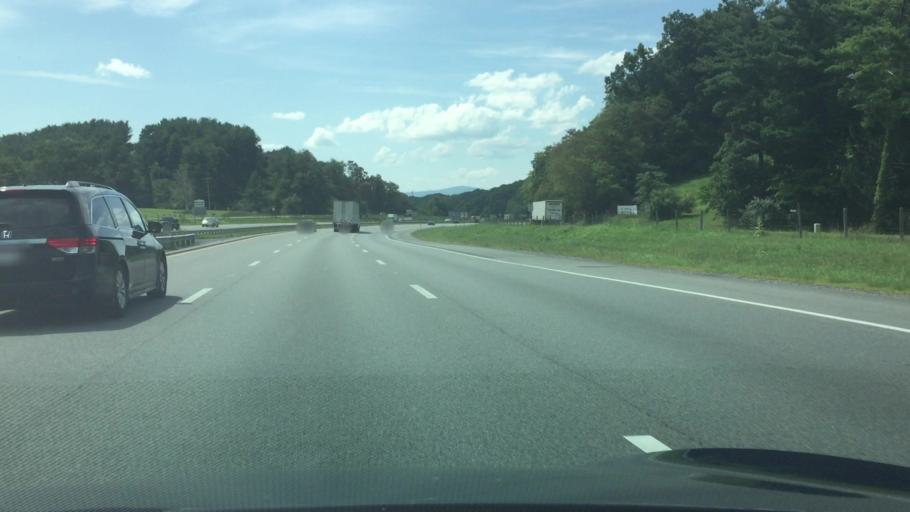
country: US
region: Virginia
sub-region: Wythe County
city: Wytheville
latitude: 36.9389
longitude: -80.9998
